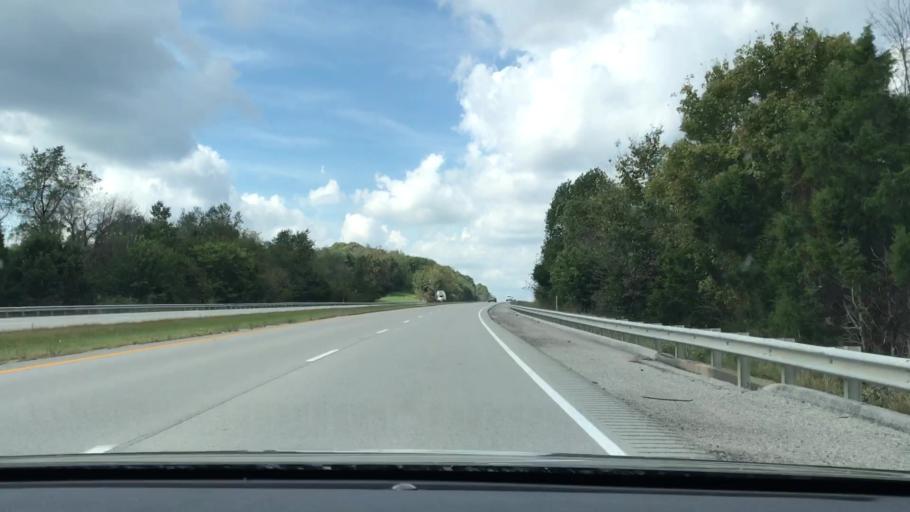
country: US
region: Kentucky
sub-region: Pulaski County
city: Somerset
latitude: 37.0935
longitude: -84.6462
